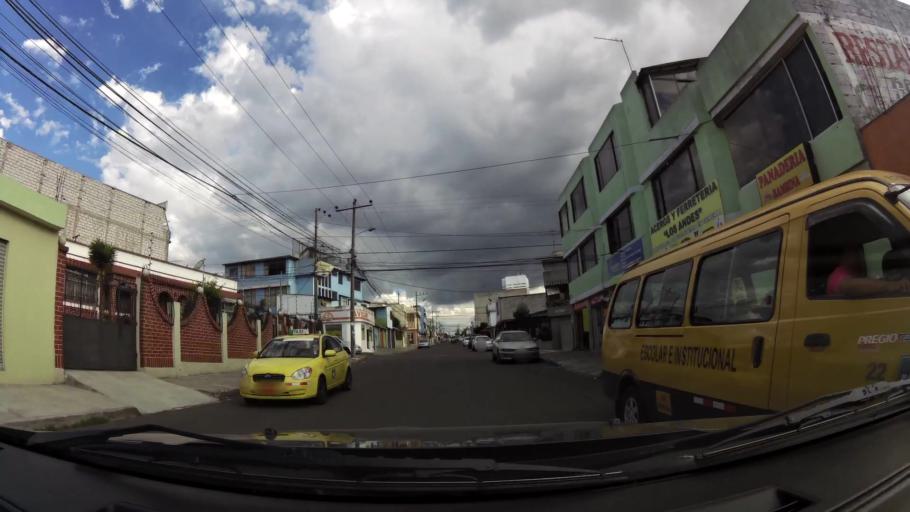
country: EC
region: Pichincha
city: Quito
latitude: -0.1163
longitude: -78.4884
